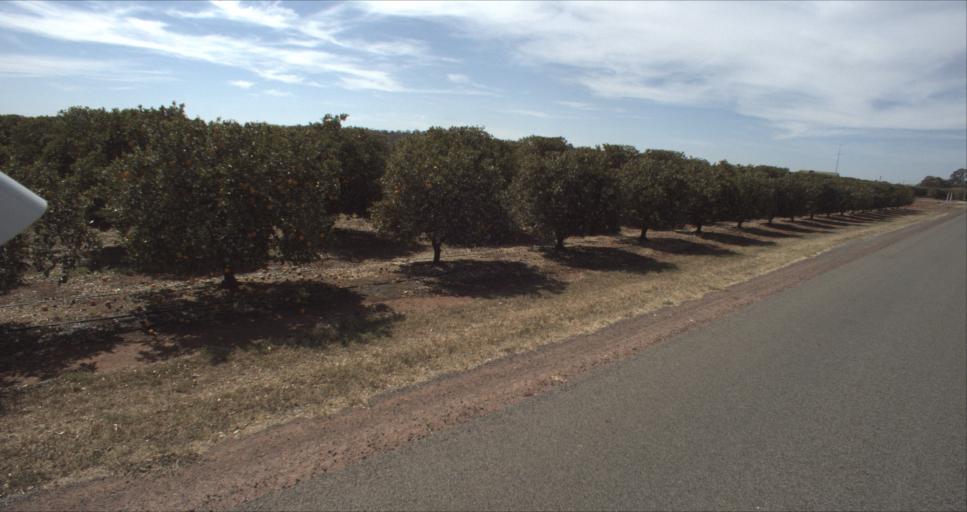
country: AU
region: New South Wales
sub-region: Leeton
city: Leeton
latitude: -34.5808
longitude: 146.4692
